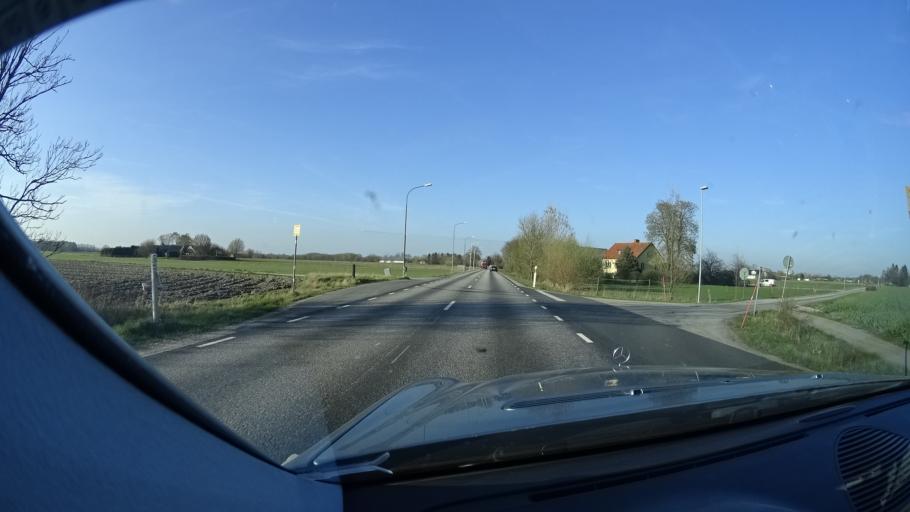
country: SE
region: Skane
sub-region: Eslovs Kommun
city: Eslov
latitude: 55.8464
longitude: 13.3418
